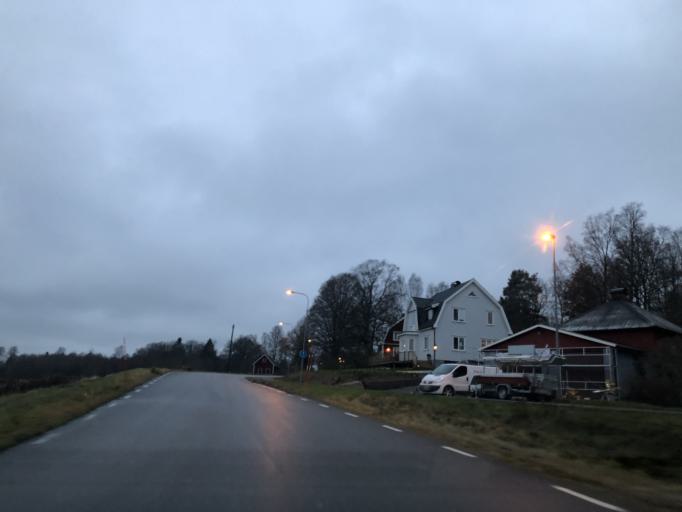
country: SE
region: Vaestra Goetaland
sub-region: Ulricehamns Kommun
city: Ulricehamn
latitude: 57.8428
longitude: 13.2789
